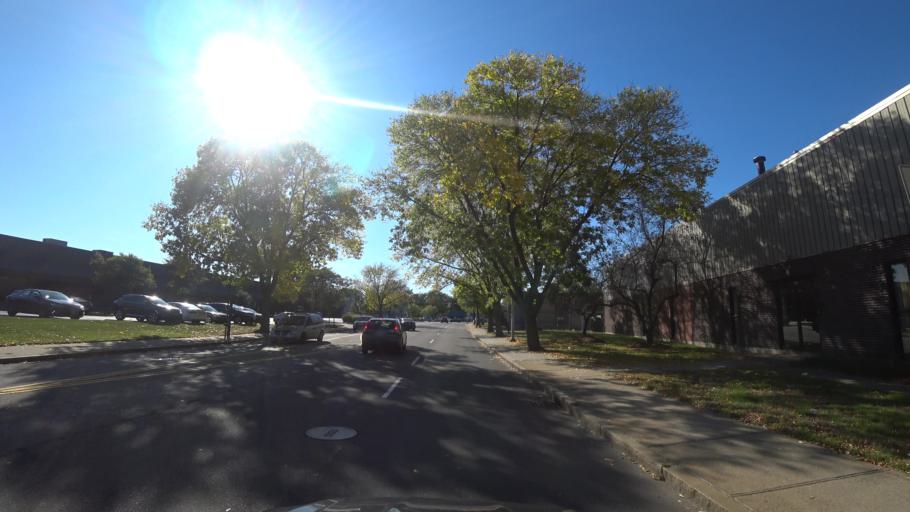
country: US
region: Massachusetts
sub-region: Middlesex County
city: Malden
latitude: 42.4179
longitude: -71.0736
